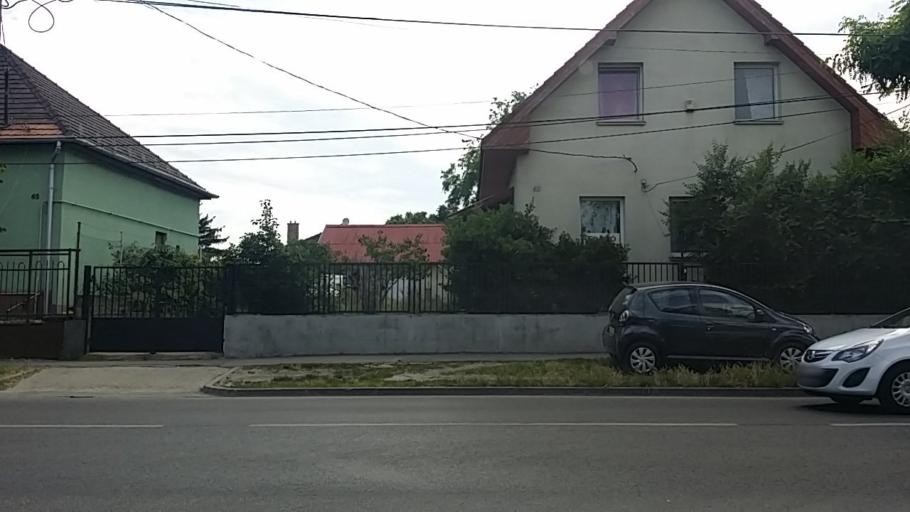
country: HU
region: Budapest
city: Budapest XXI. keruelet
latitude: 47.4173
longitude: 19.0775
